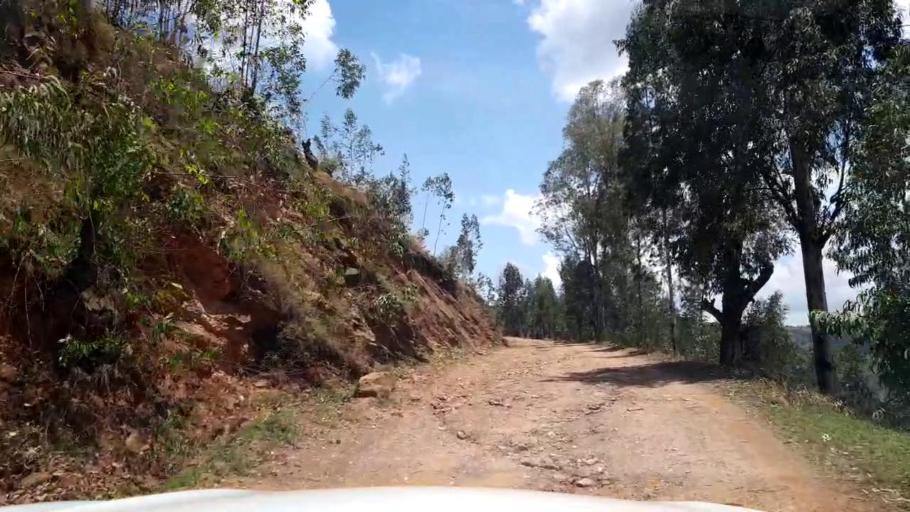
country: RW
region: Northern Province
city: Byumba
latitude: -1.5269
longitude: 30.1725
